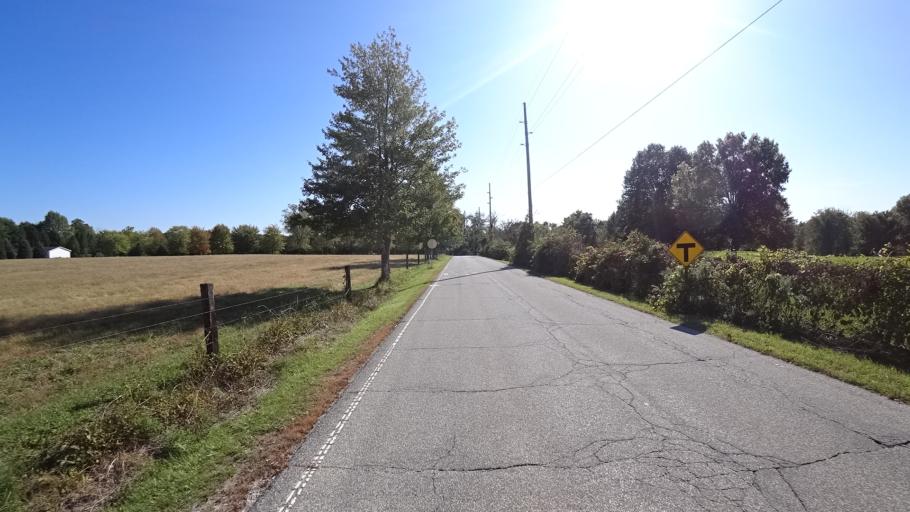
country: US
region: Indiana
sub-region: LaPorte County
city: Trail Creek
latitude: 41.7106
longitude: -86.8405
